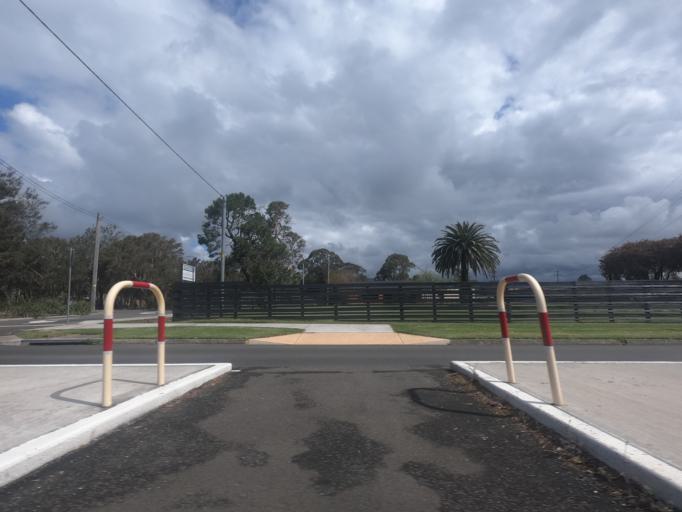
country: AU
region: New South Wales
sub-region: Wollongong
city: Dapto
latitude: -34.4920
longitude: 150.7858
